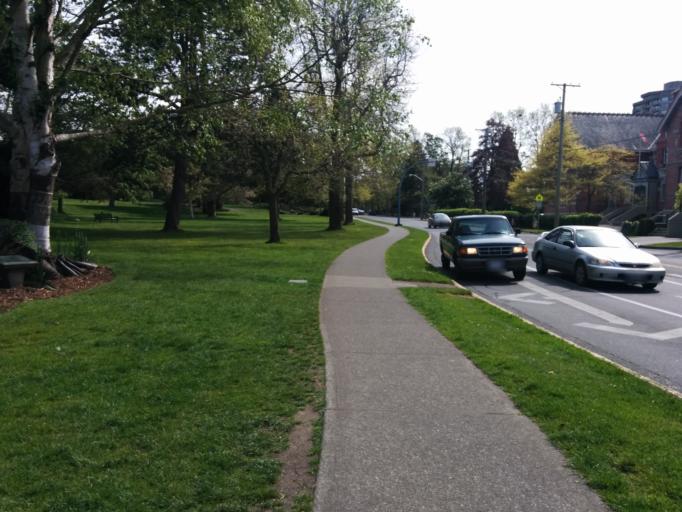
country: CA
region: British Columbia
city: Victoria
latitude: 48.4183
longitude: -123.3656
